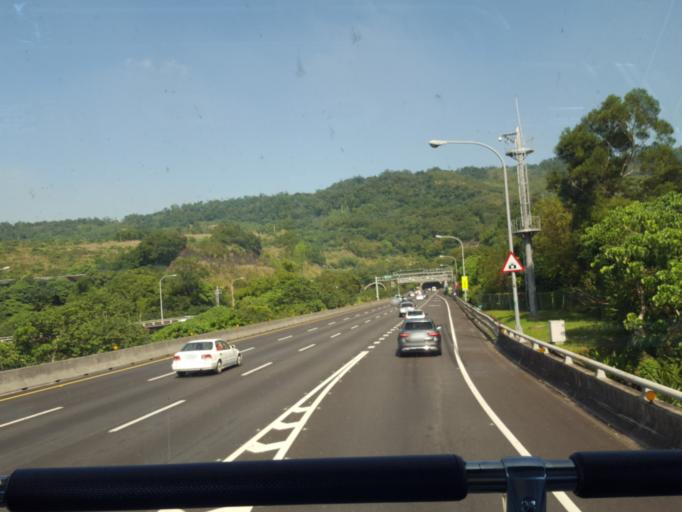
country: TW
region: Taipei
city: Taipei
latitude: 25.0047
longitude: 121.5959
